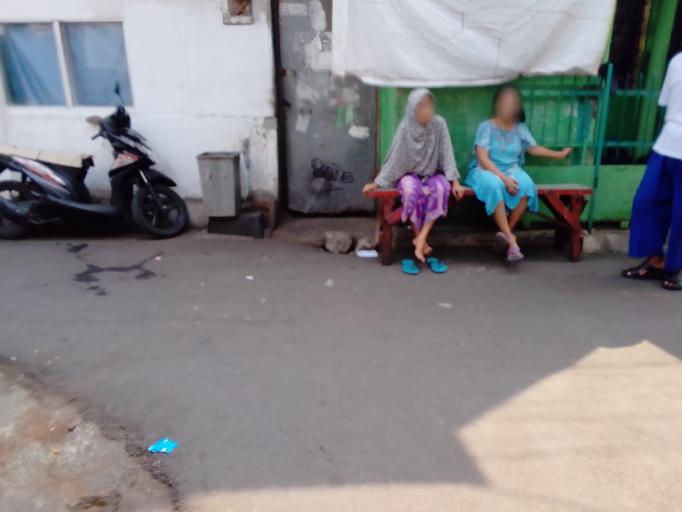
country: ID
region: Jakarta Raya
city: Jakarta
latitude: -6.2097
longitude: 106.7931
